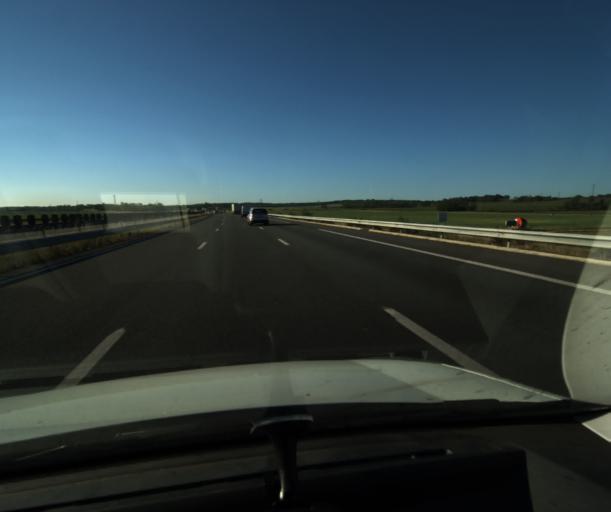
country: FR
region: Midi-Pyrenees
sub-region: Departement du Tarn-et-Garonne
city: Grisolles
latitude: 43.8497
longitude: 1.3200
